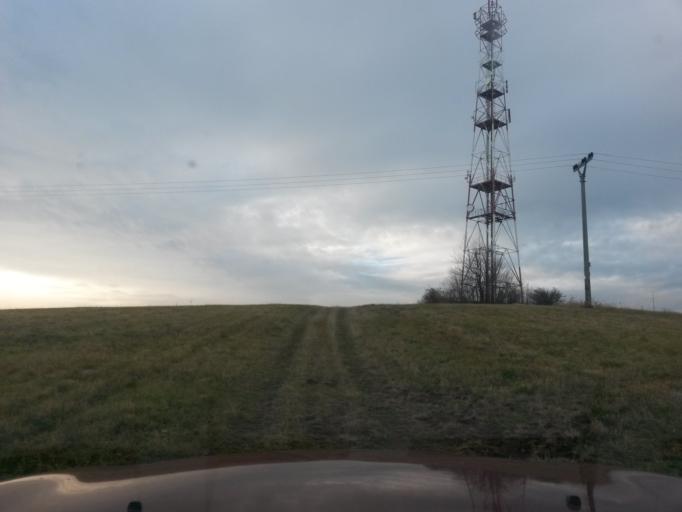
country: SK
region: Kosicky
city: Kosice
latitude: 48.7691
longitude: 21.2101
